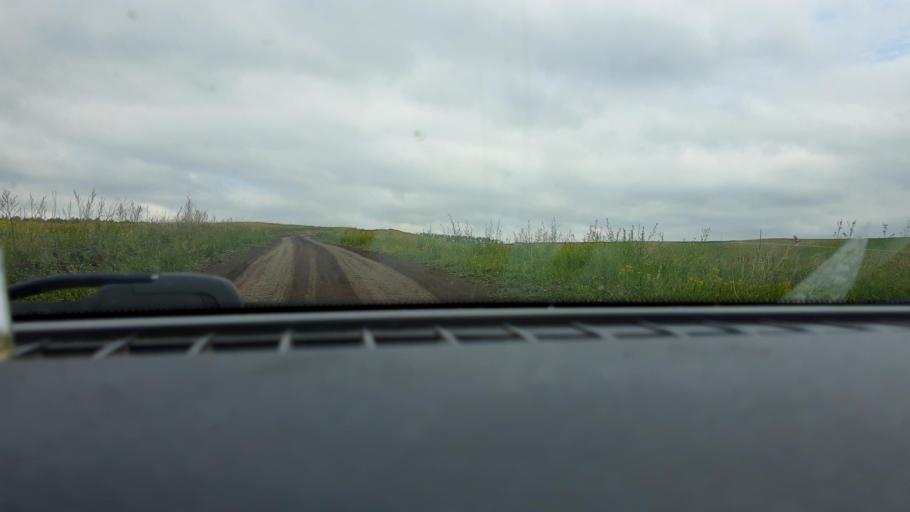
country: RU
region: Bashkortostan
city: Chishmy
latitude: 54.6890
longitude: 55.4838
